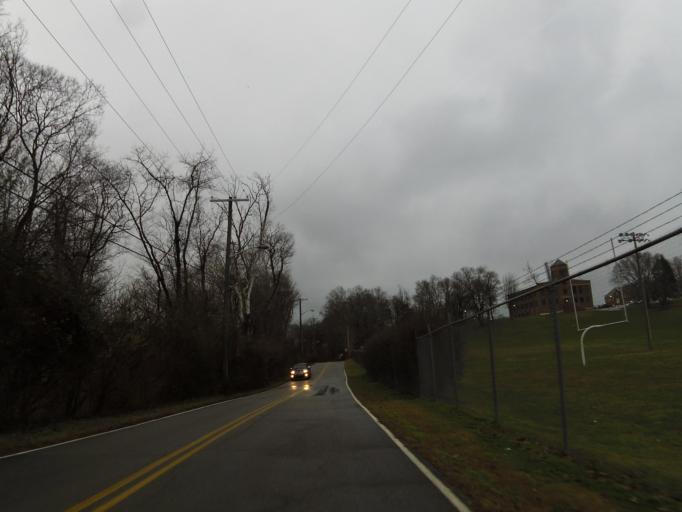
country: US
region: Tennessee
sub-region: Knox County
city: Knoxville
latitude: 35.9610
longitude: -83.8798
